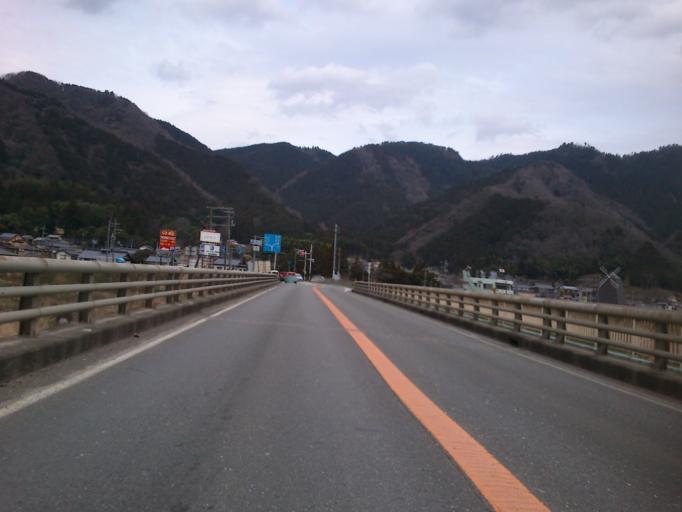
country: JP
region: Kyoto
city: Fukuchiyama
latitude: 35.3334
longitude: 135.0986
